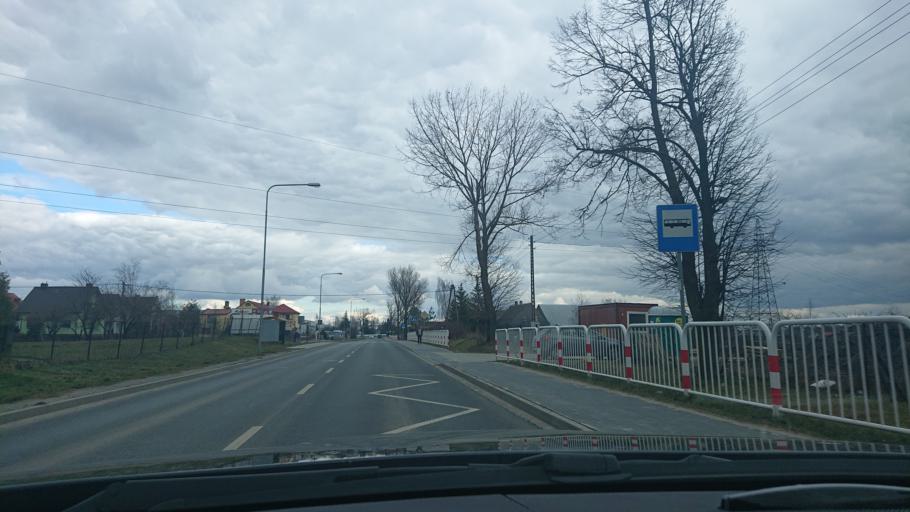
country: PL
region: Greater Poland Voivodeship
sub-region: Powiat gnieznienski
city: Gniezno
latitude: 52.5408
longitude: 17.6432
